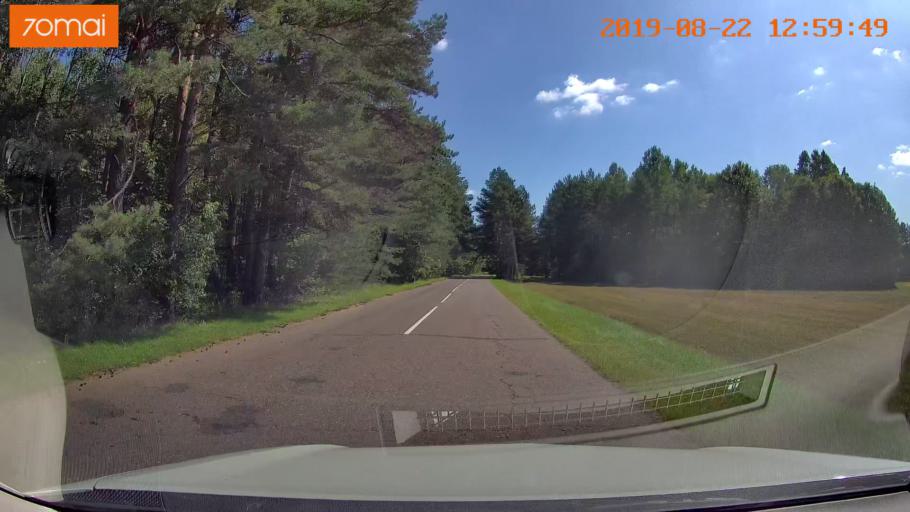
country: BY
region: Minsk
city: Prawdzinski
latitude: 53.4214
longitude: 27.7991
